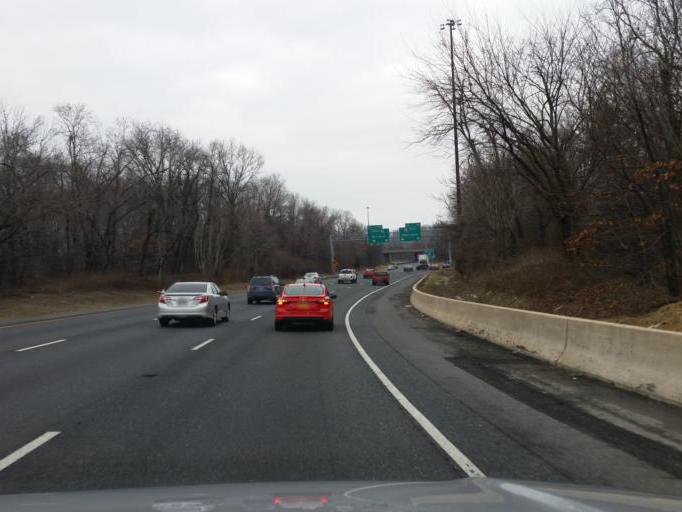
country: US
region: Maryland
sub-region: Baltimore County
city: Arbutus
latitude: 39.2530
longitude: -76.6843
